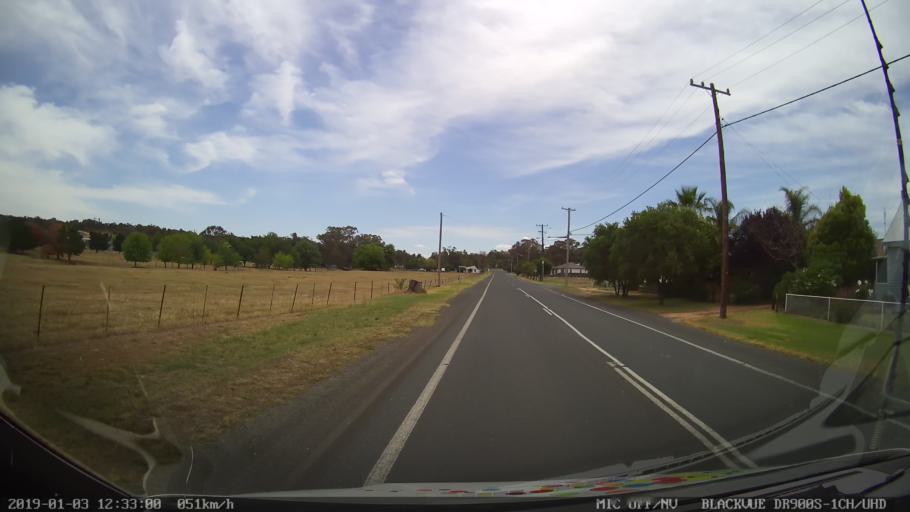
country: AU
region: New South Wales
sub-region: Weddin
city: Grenfell
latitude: -33.8885
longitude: 148.1624
